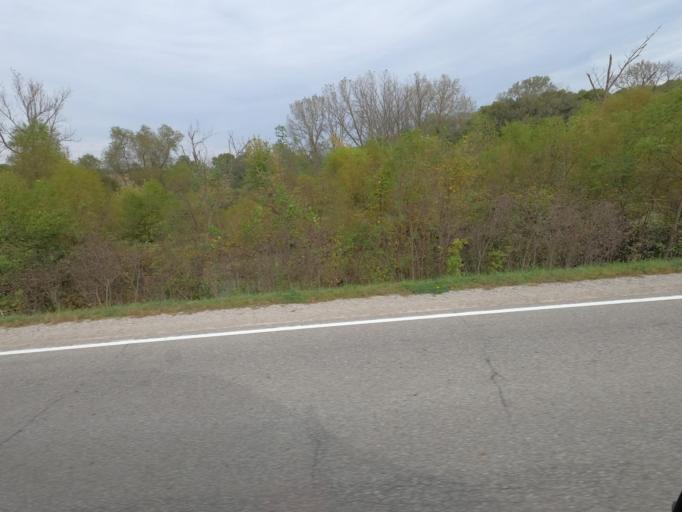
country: US
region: Iowa
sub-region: Jefferson County
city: Fairfield
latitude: 40.8745
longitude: -92.1544
